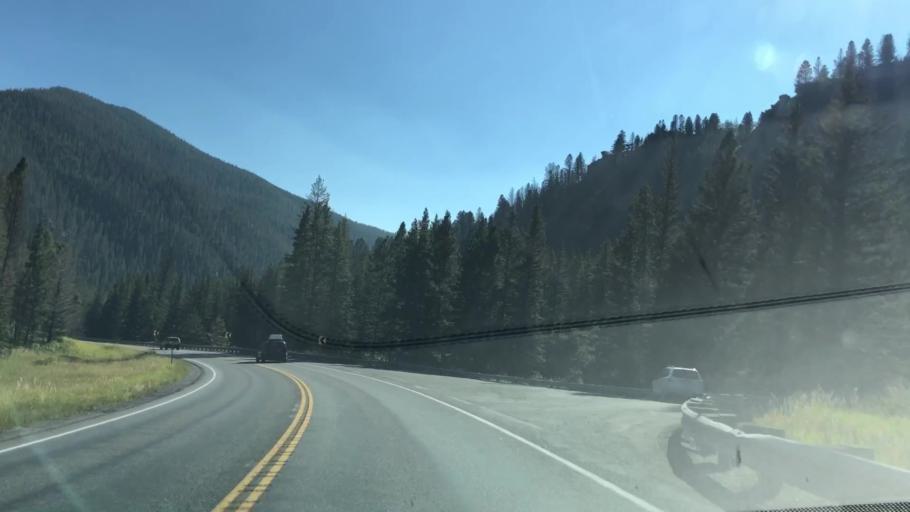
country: US
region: Montana
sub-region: Gallatin County
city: Big Sky
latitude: 45.3069
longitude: -111.1963
